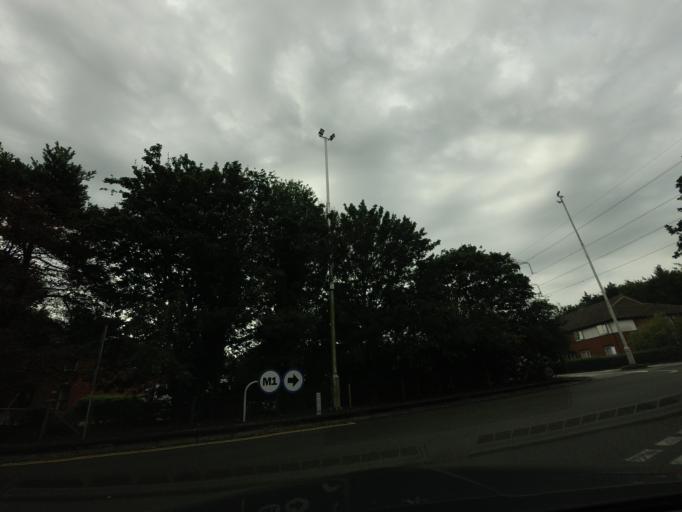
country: GB
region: England
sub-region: Central Bedfordshire
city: Harlington
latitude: 51.9480
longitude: -0.4992
